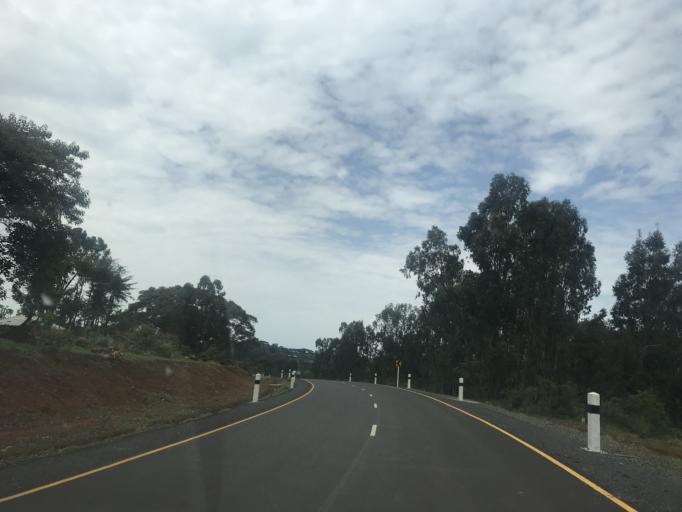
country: ET
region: Oromiya
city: Shambu
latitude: 9.8762
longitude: 36.6737
